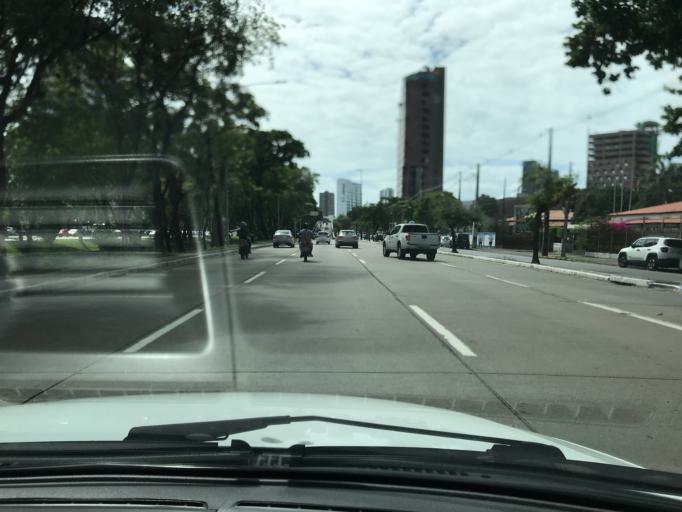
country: BR
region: Pernambuco
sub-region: Recife
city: Recife
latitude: -8.0480
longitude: -34.8921
